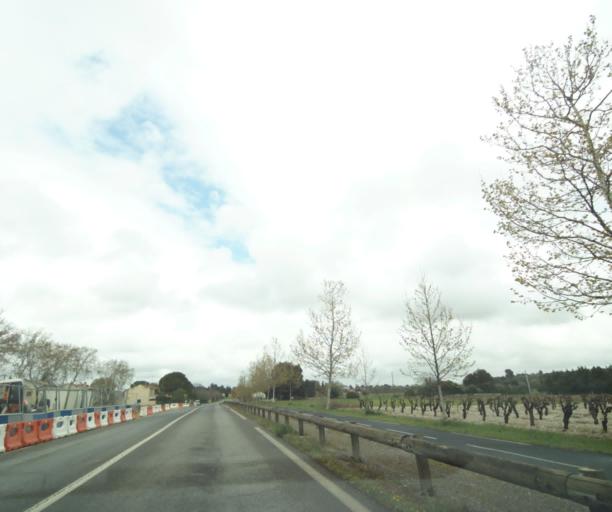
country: FR
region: Languedoc-Roussillon
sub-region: Departement de l'Herault
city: Cournonsec
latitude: 43.5458
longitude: 3.7059
